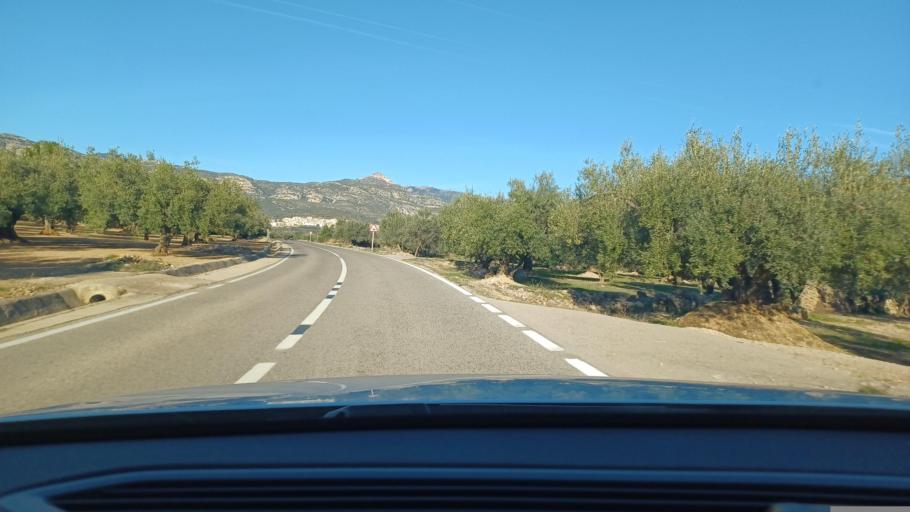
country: ES
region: Catalonia
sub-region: Provincia de Tarragona
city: Mas de Barberans
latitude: 40.7225
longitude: 0.3951
